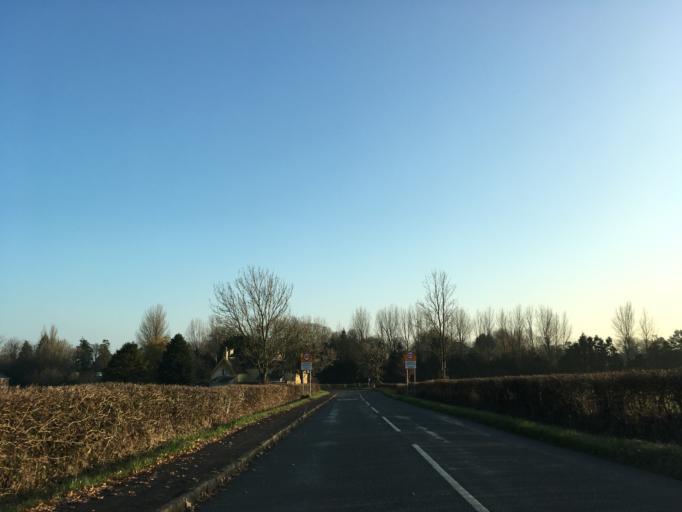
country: GB
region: England
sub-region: Wiltshire
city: Nettleton
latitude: 51.5317
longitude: -2.2801
